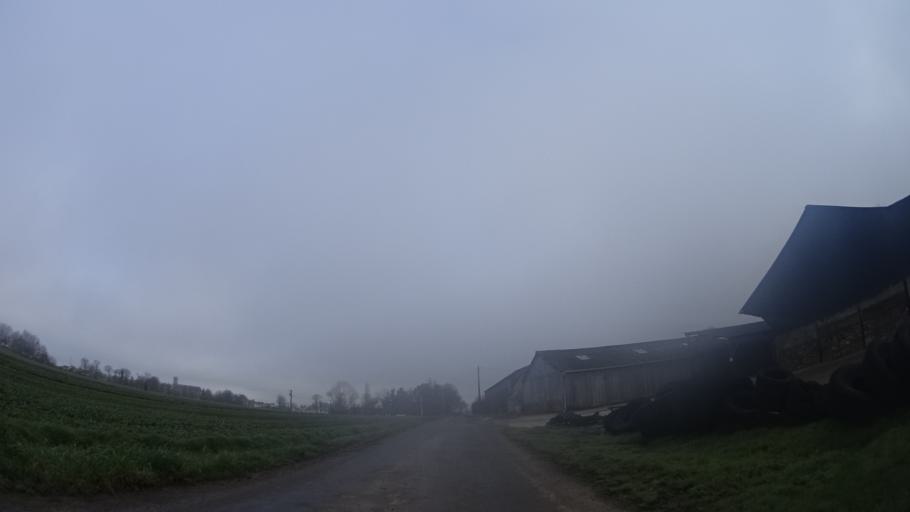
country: FR
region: Brittany
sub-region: Departement d'Ille-et-Vilaine
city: Saint-Domineuc
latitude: 48.3334
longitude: -1.9285
